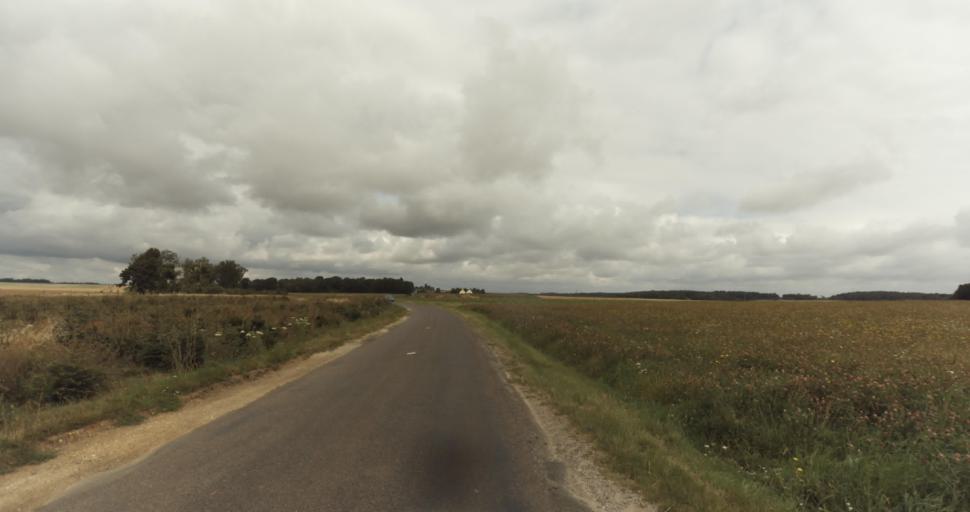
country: FR
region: Haute-Normandie
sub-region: Departement de l'Eure
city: Menilles
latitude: 48.9530
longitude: 1.3024
